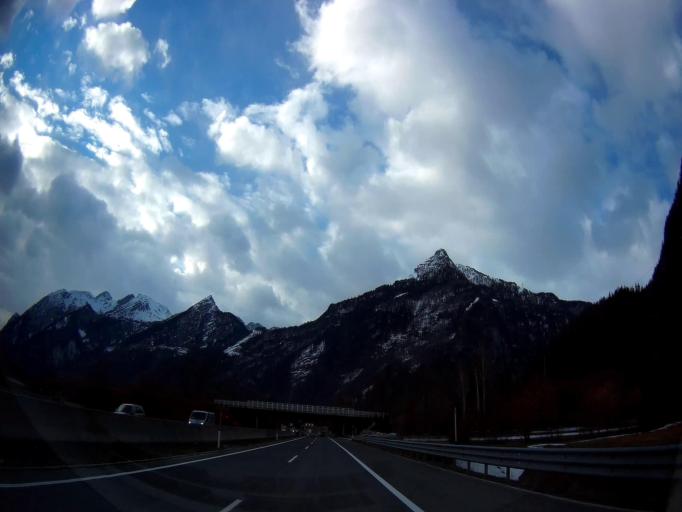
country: AT
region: Salzburg
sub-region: Politischer Bezirk Hallein
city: Golling an der Salzach
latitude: 47.5937
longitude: 13.1493
